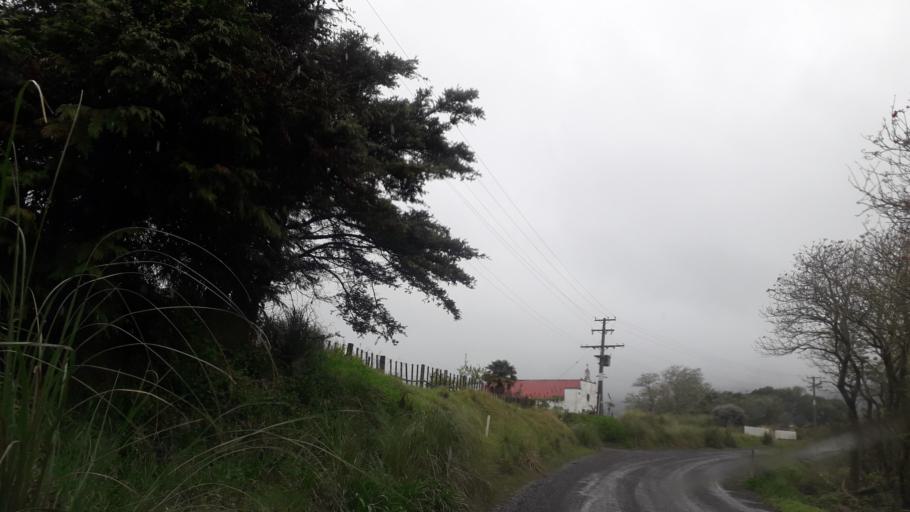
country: NZ
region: Northland
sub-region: Far North District
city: Kaitaia
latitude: -35.4052
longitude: 173.3760
